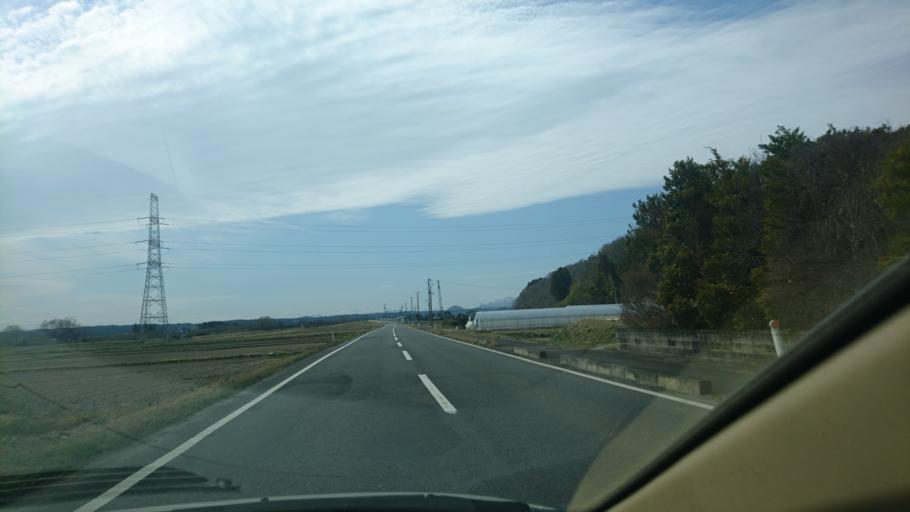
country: JP
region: Miyagi
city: Furukawa
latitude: 38.7455
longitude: 140.9776
